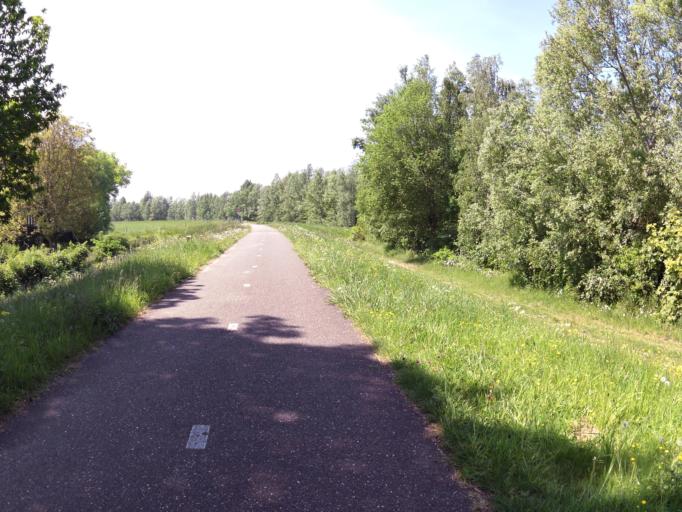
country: NL
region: Gelderland
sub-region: Gemeente Neerijnen
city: Neerijnen
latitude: 51.8159
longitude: 5.3207
